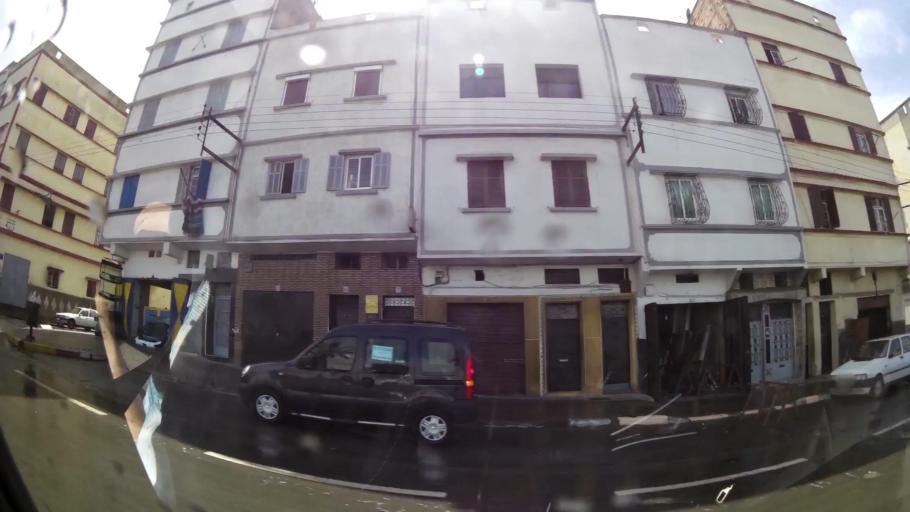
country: MA
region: Grand Casablanca
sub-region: Casablanca
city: Casablanca
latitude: 33.5477
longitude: -7.5654
